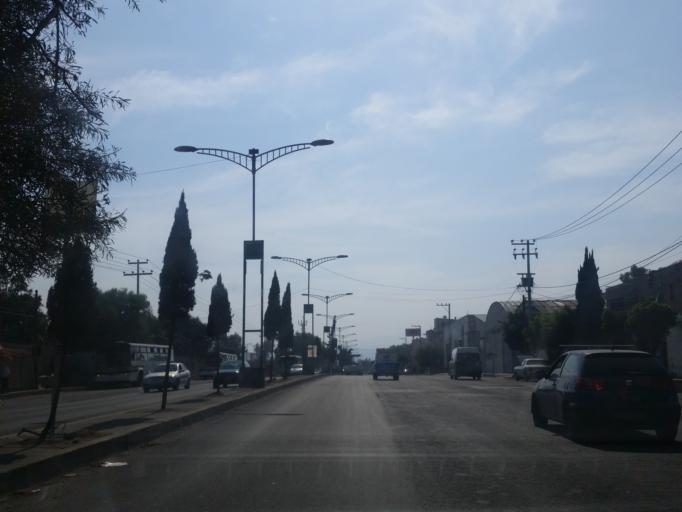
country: MX
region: Mexico
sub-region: La Paz
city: San Isidro
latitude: 19.3213
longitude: -98.9593
